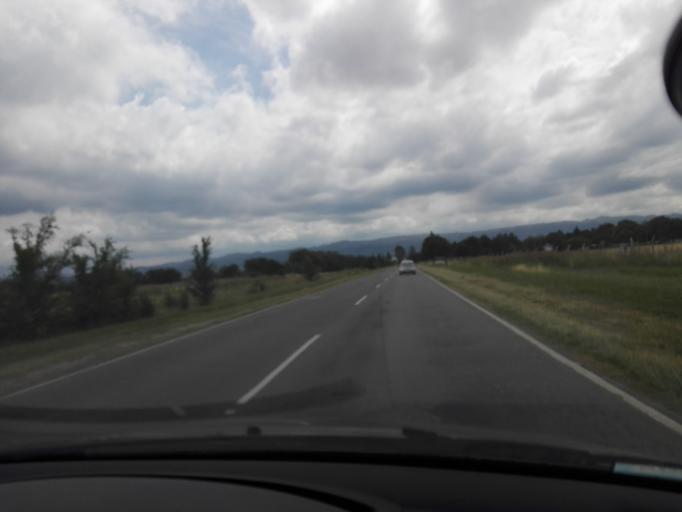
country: AR
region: Cordoba
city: Alta Gracia
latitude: -31.6582
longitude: -64.3940
